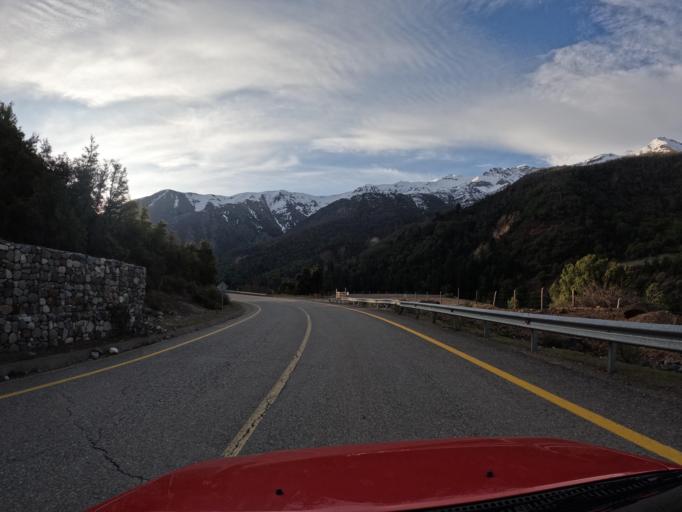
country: CL
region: Maule
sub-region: Provincia de Linares
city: Colbun
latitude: -35.8254
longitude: -70.7667
